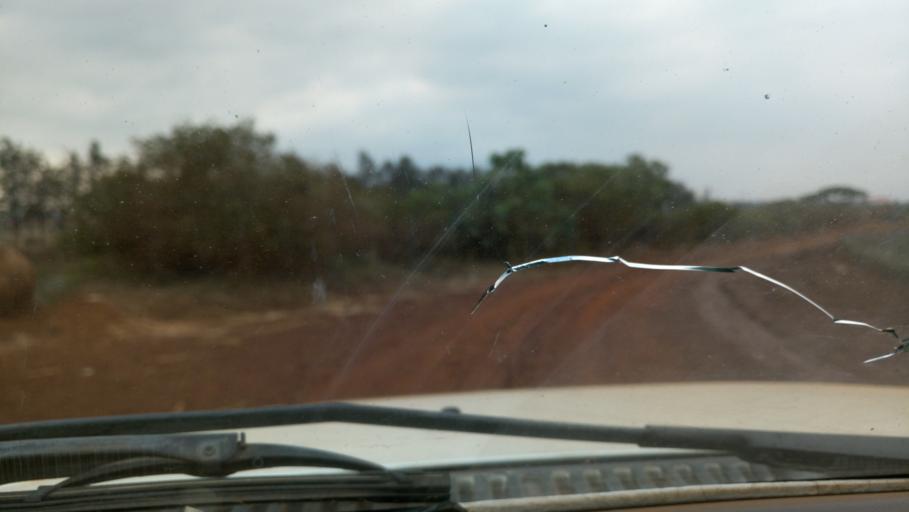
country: KE
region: Nairobi Area
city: Thika
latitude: -0.9666
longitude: 37.0994
